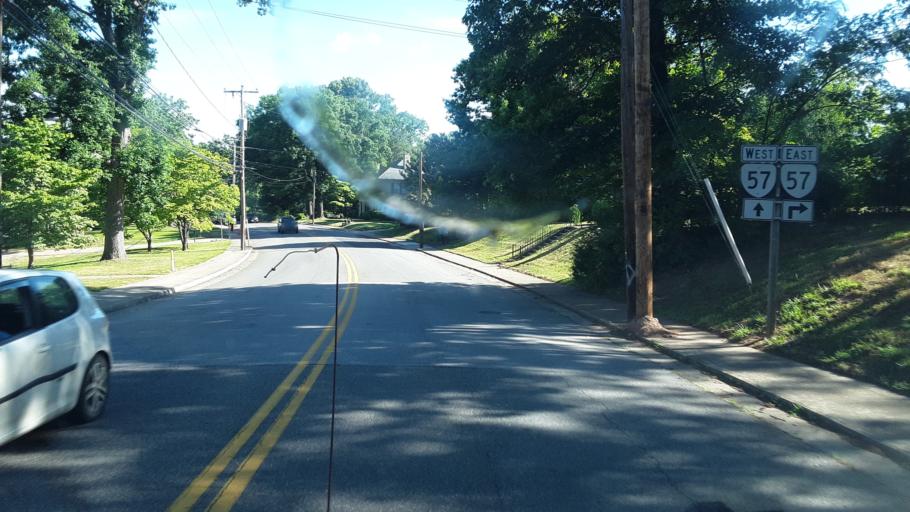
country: US
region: Virginia
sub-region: Pittsylvania County
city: Chatham
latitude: 36.8202
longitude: -79.3963
